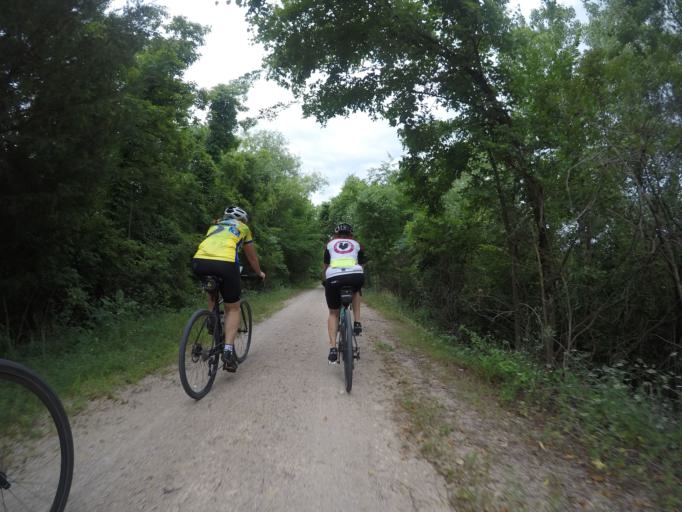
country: US
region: Kansas
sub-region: Anderson County
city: Garnett
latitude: 38.2572
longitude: -95.2509
